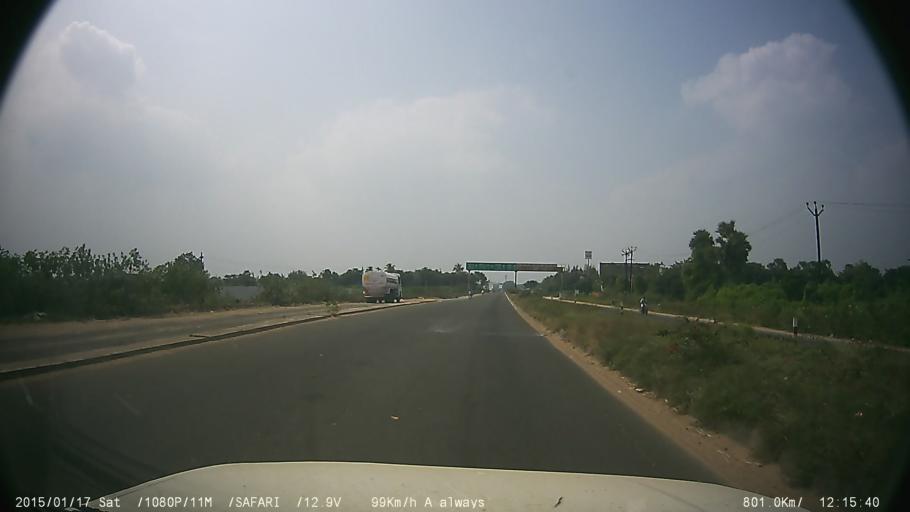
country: IN
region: Tamil Nadu
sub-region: Kancheepuram
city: Sriperumbudur
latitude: 12.9204
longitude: 79.8711
